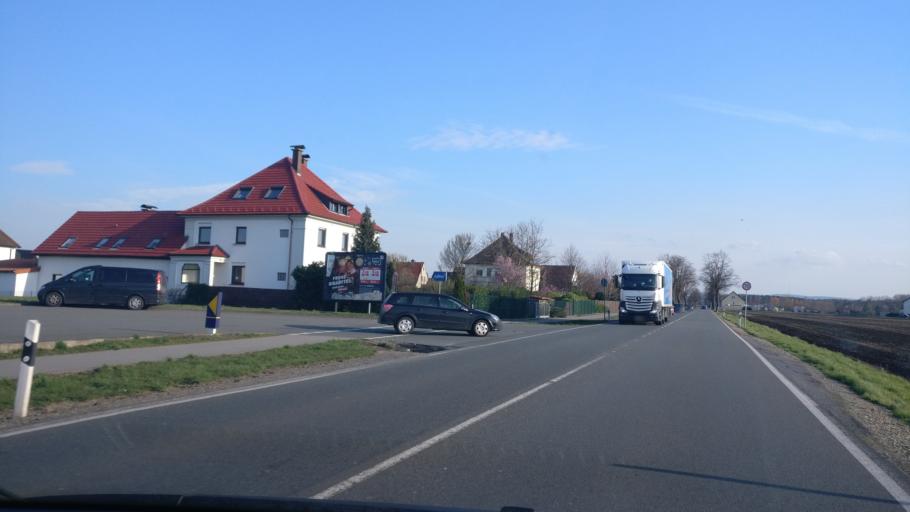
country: DE
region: North Rhine-Westphalia
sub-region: Regierungsbezirk Detmold
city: Lage
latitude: 52.0232
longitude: 8.7614
